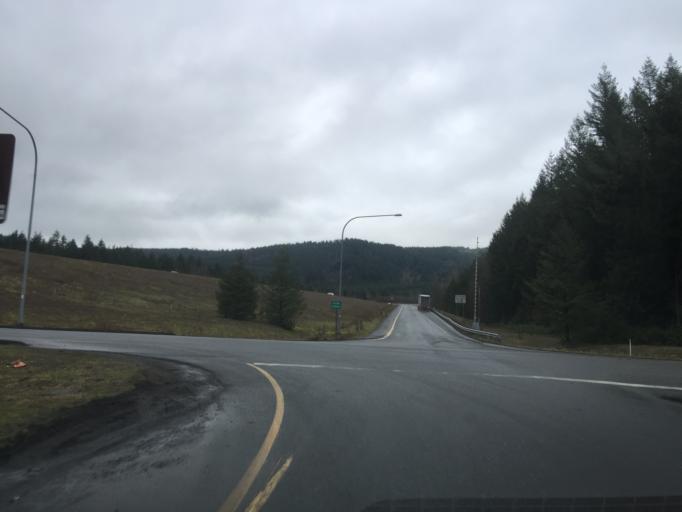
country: US
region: Washington
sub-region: King County
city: Tanner
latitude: 47.4641
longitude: -121.7166
